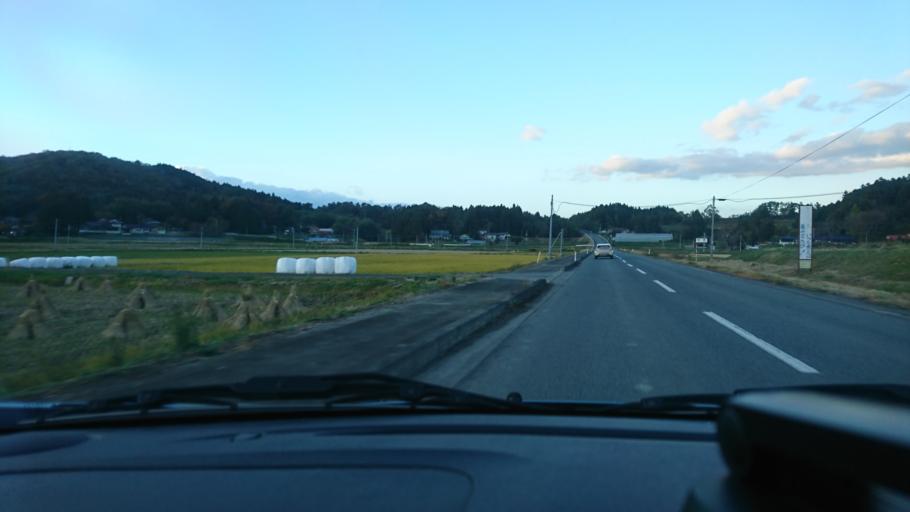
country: JP
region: Iwate
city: Ichinoseki
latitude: 38.7605
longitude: 141.2382
